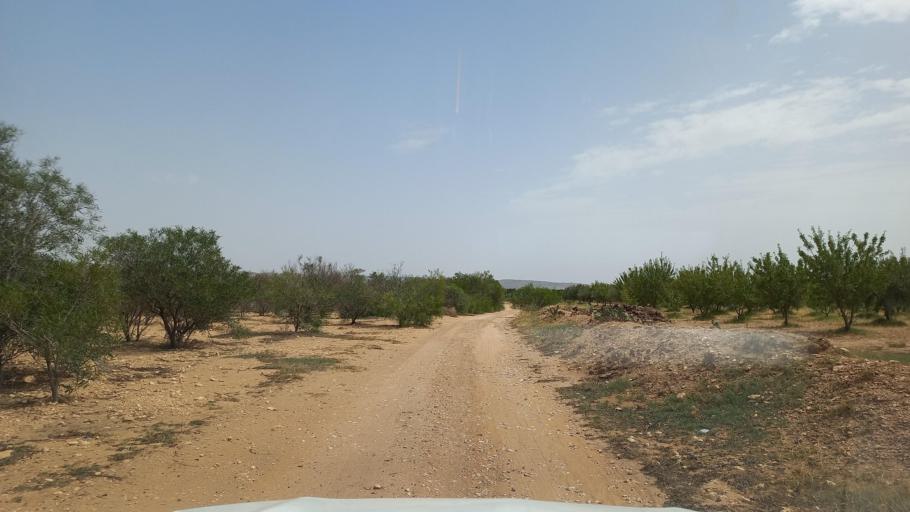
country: TN
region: Al Qasrayn
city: Kasserine
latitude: 35.2930
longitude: 9.0129
